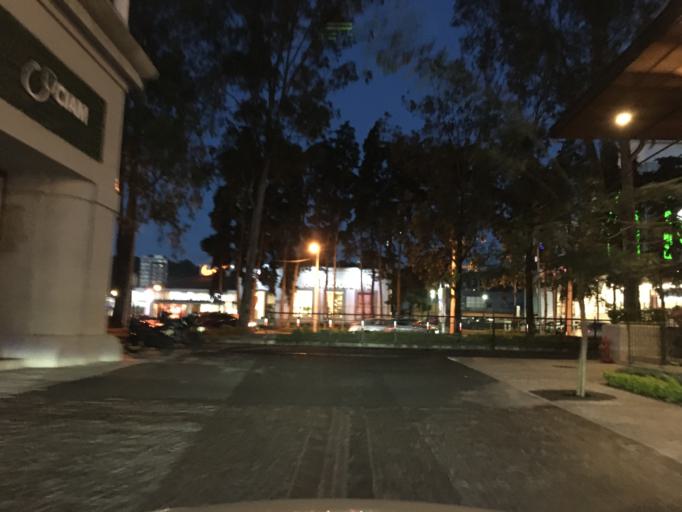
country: GT
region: Guatemala
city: Guatemala City
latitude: 14.6104
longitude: -90.4842
